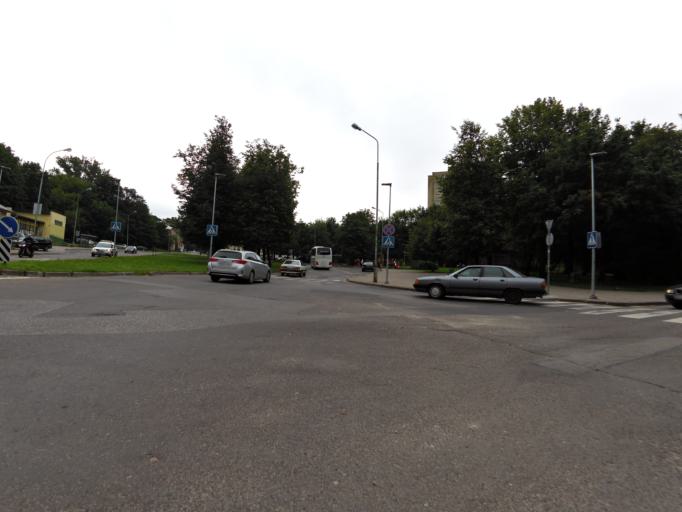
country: LT
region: Vilnius County
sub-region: Vilnius
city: Vilnius
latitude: 54.6718
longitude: 25.2908
